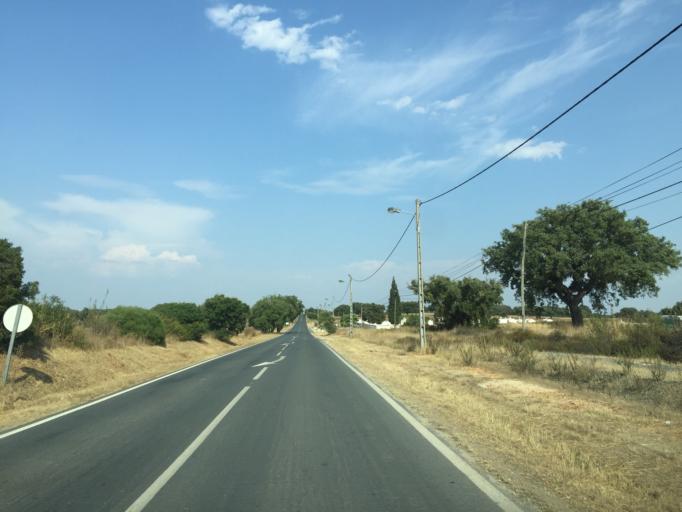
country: PT
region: Setubal
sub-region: Grandola
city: Grandola
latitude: 38.0090
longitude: -8.4053
